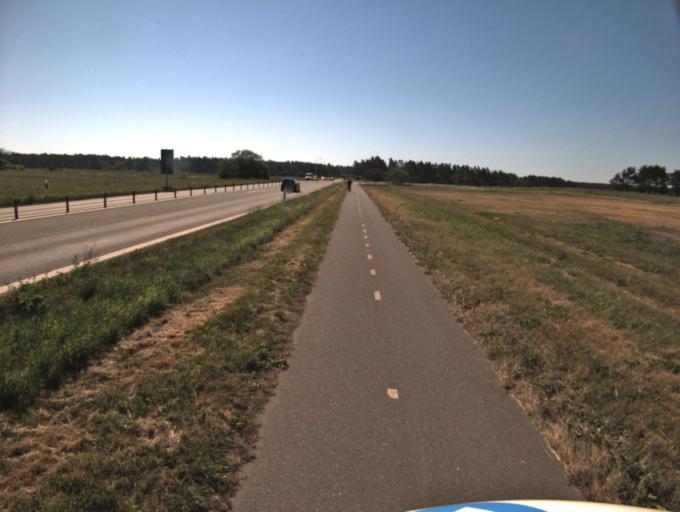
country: SE
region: Skane
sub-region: Kristianstads Kommun
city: Ahus
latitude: 55.9684
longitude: 14.2762
